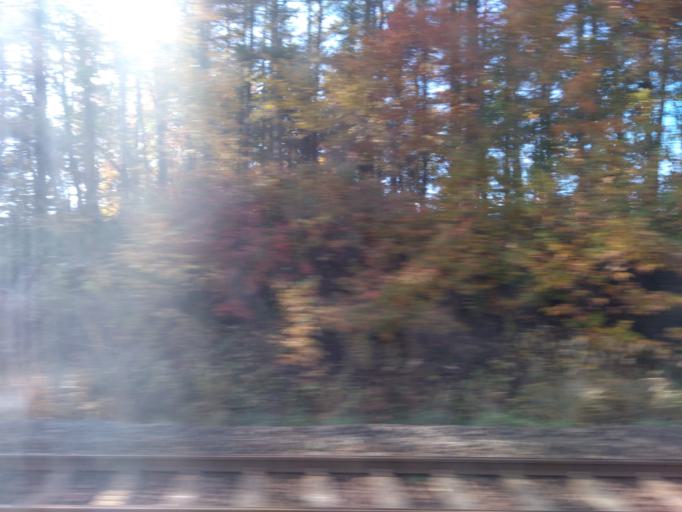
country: JP
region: Hokkaido
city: Kitahiroshima
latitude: 42.9312
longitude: 141.5726
